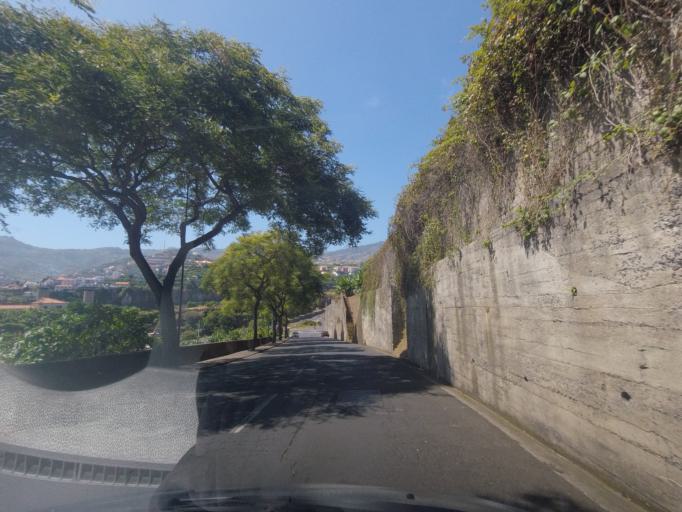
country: PT
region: Madeira
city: Camara de Lobos
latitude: 32.6461
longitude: -16.9655
